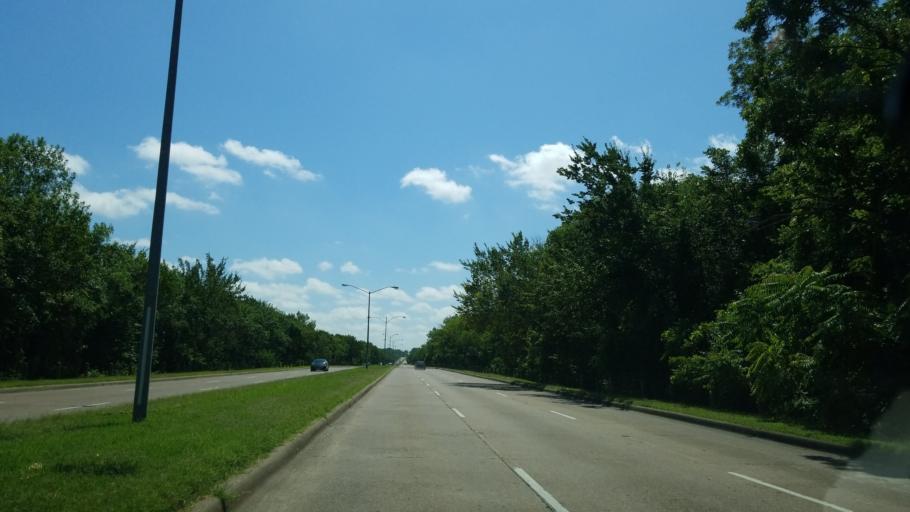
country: US
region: Texas
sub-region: Dallas County
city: Dallas
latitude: 32.7492
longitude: -96.7209
